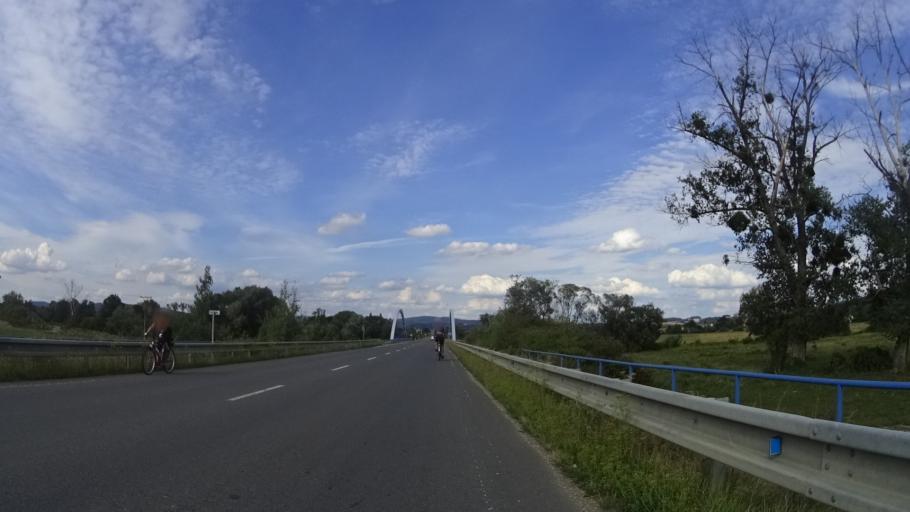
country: CZ
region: Olomoucky
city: Moravicany
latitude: 49.7837
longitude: 16.9577
